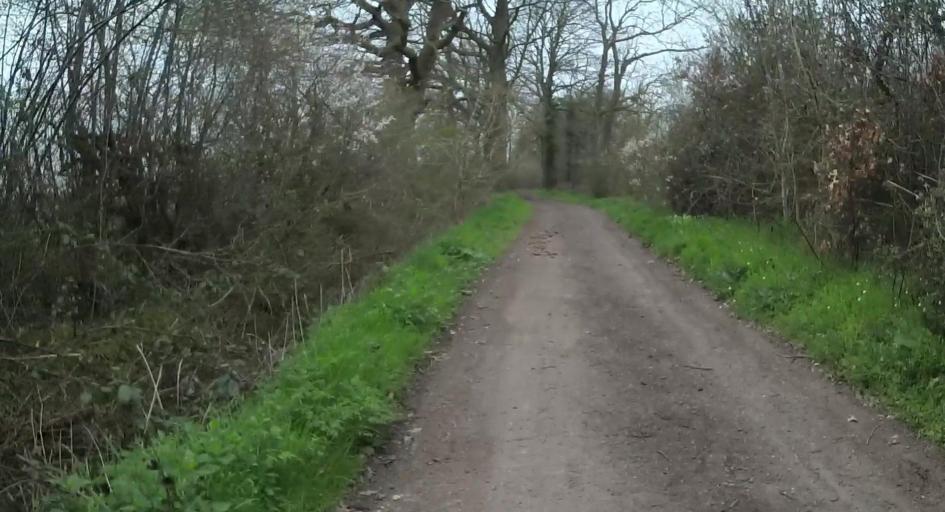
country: GB
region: England
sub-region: West Berkshire
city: Arborfield
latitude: 51.4099
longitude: -0.9088
